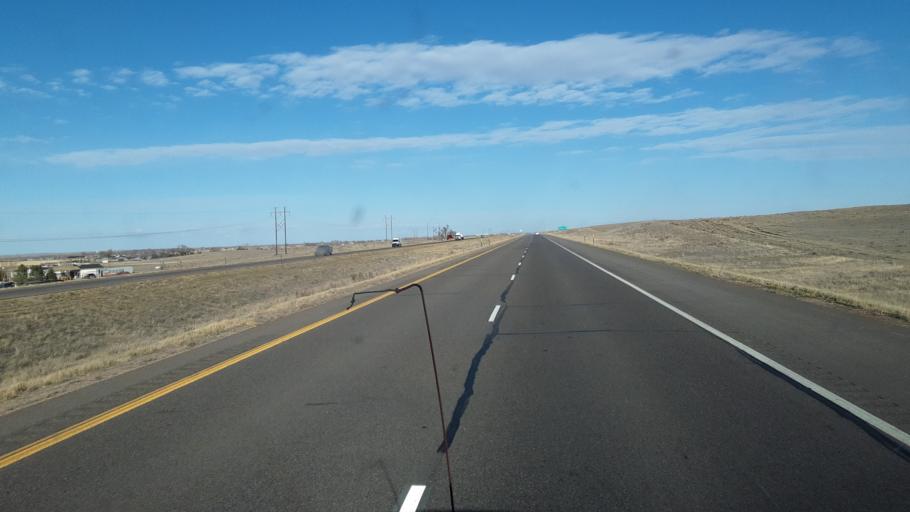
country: US
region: Colorado
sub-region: Morgan County
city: Brush
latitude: 40.2955
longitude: -103.5372
